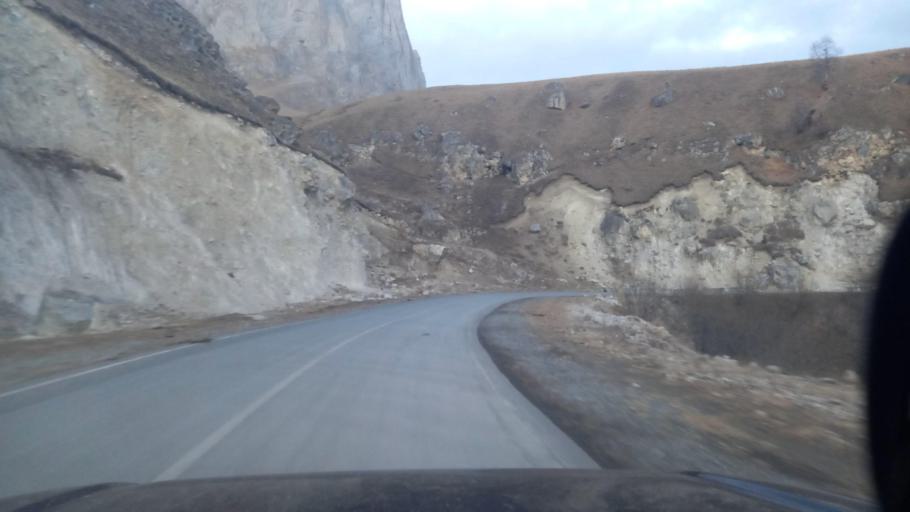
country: RU
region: Ingushetiya
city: Dzhayrakh
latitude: 42.8208
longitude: 44.8328
